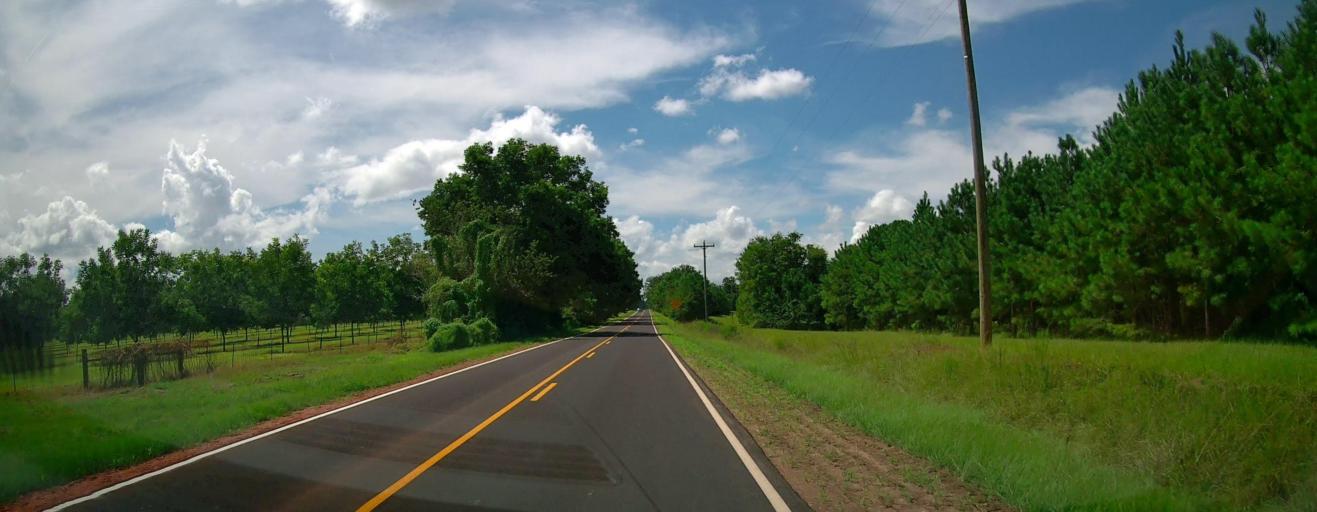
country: US
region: Georgia
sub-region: Macon County
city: Marshallville
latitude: 32.4725
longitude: -83.8744
